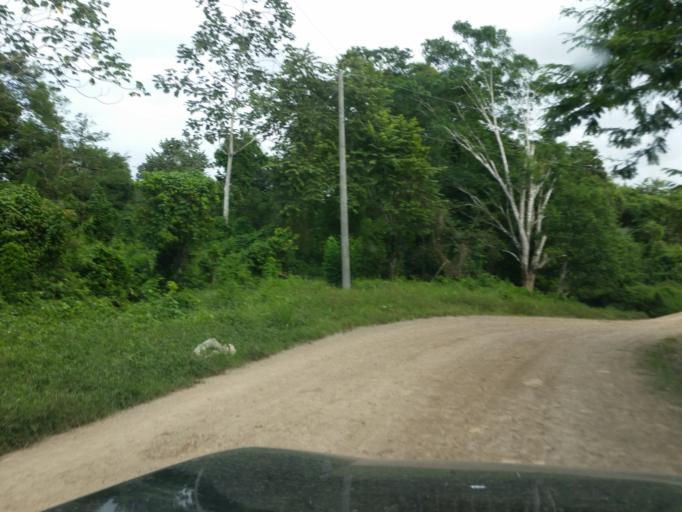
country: CR
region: Alajuela
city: Los Chiles
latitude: 11.1203
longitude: -84.6018
